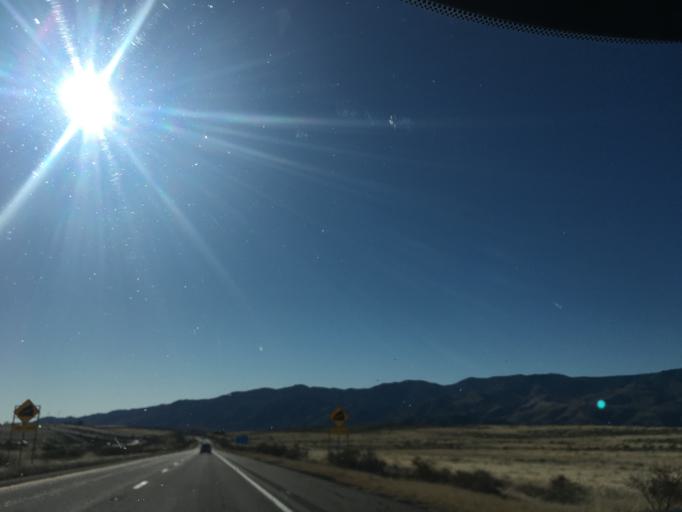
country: US
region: Arizona
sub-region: Yavapai County
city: Cordes Lakes
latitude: 34.2046
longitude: -112.1232
